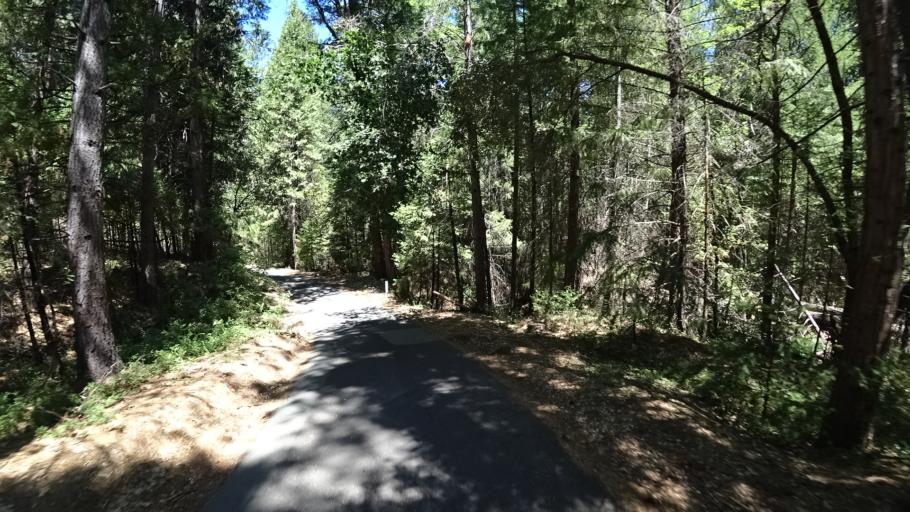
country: US
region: California
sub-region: Amador County
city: Pioneer
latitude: 38.3553
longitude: -120.5564
